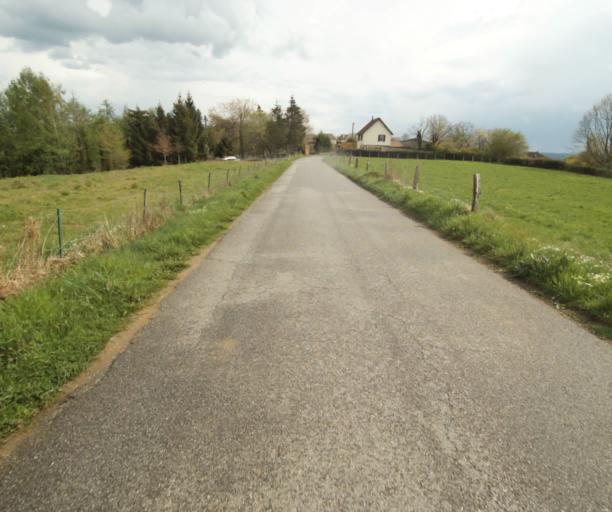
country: FR
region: Limousin
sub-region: Departement de la Correze
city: Tulle
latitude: 45.2792
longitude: 1.7486
